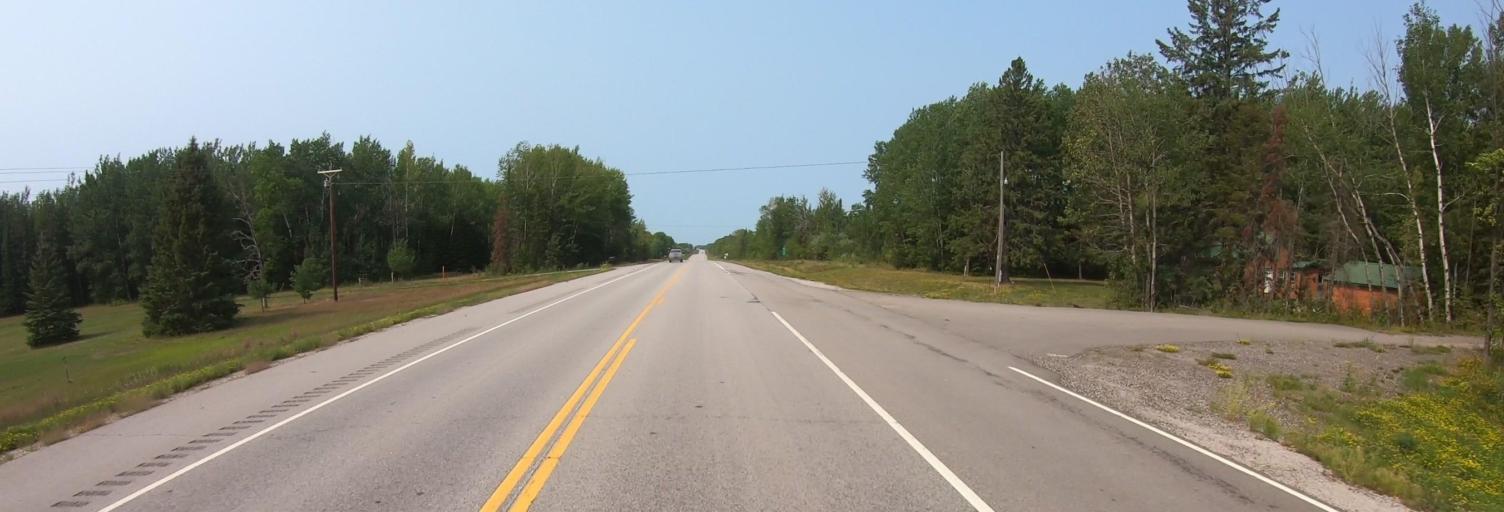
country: CA
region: Ontario
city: Fort Frances
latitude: 48.4088
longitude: -93.0868
